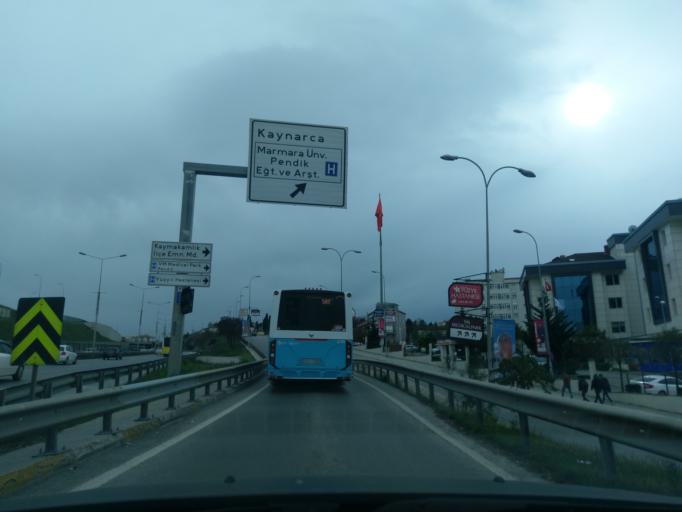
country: TR
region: Istanbul
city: Pendik
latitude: 40.8835
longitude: 29.2456
